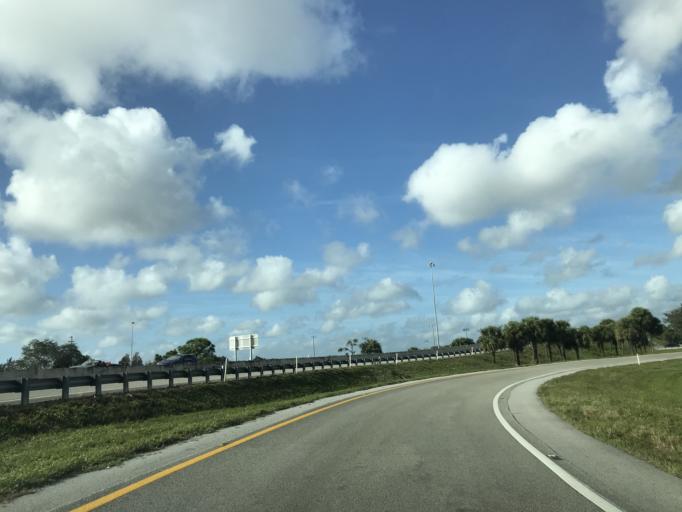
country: US
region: Florida
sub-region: Broward County
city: Coconut Creek
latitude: 26.2708
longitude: -80.1664
